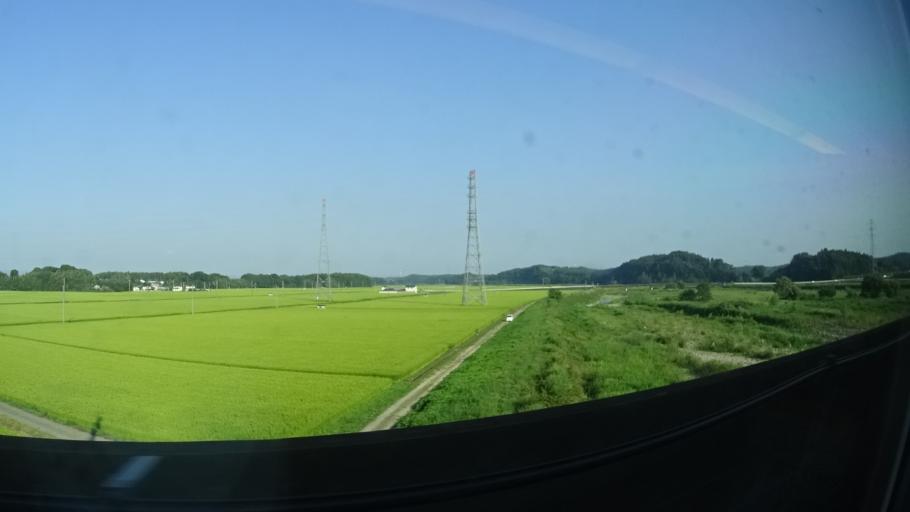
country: JP
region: Tochigi
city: Yaita
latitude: 36.8303
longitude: 139.9612
